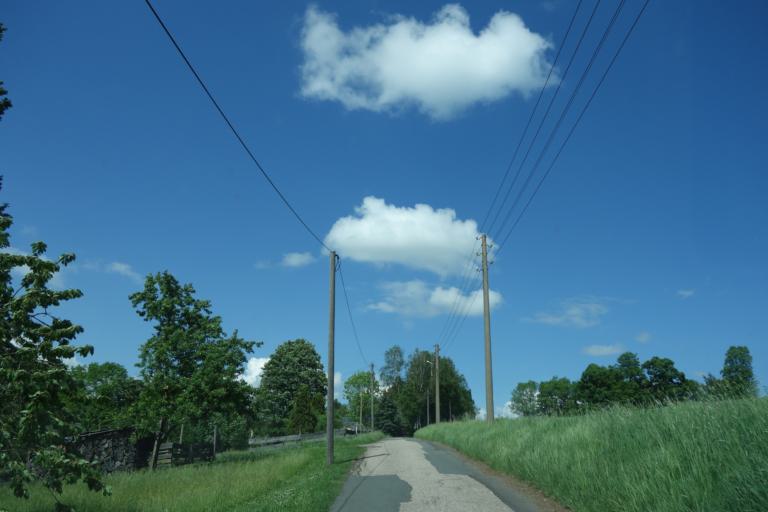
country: DE
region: Saxony
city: Eppendorf
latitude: 50.8033
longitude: 13.2832
